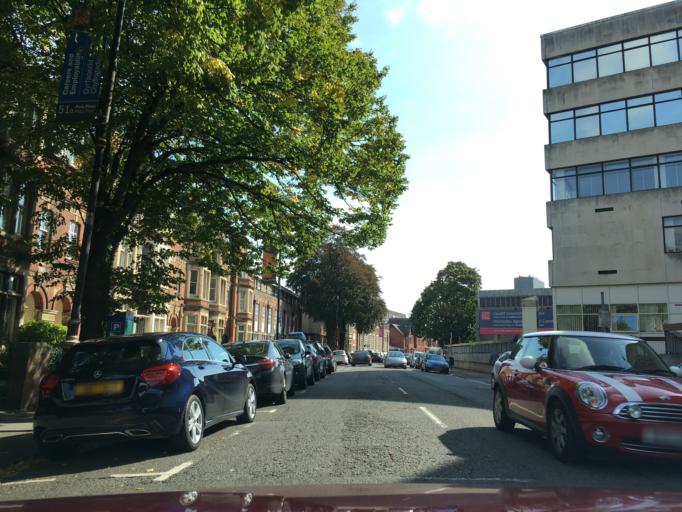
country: GB
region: Wales
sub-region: Cardiff
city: Cardiff
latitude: 51.4890
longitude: -3.1806
